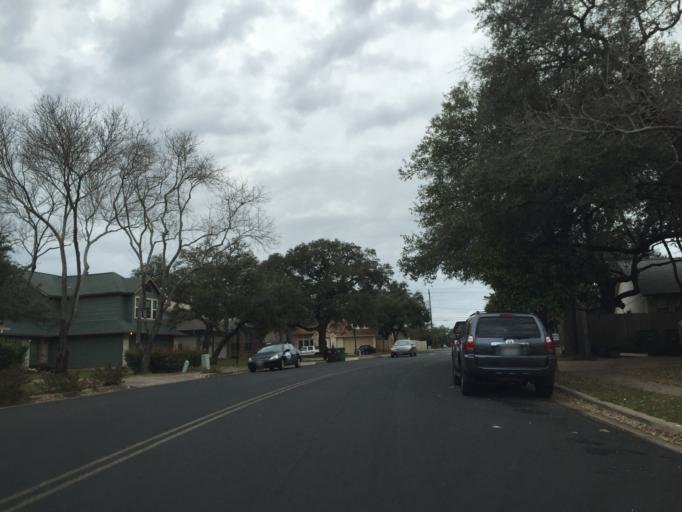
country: US
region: Texas
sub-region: Williamson County
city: Jollyville
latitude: 30.4451
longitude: -97.7482
